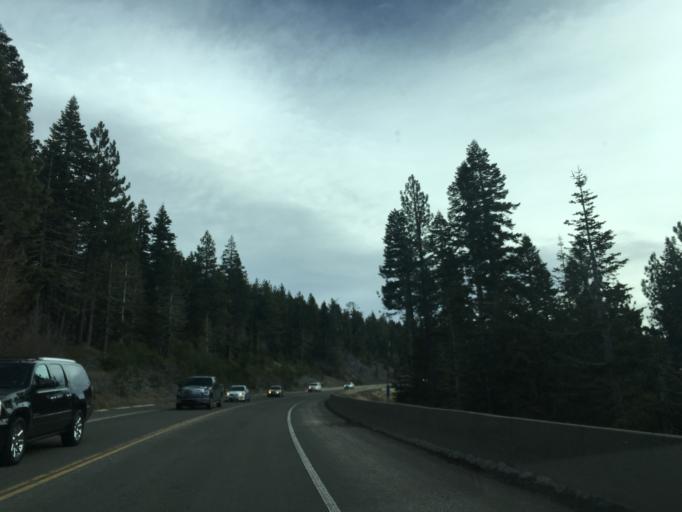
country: US
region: Nevada
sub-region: Washoe County
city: Incline Village
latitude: 39.2678
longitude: -119.9345
